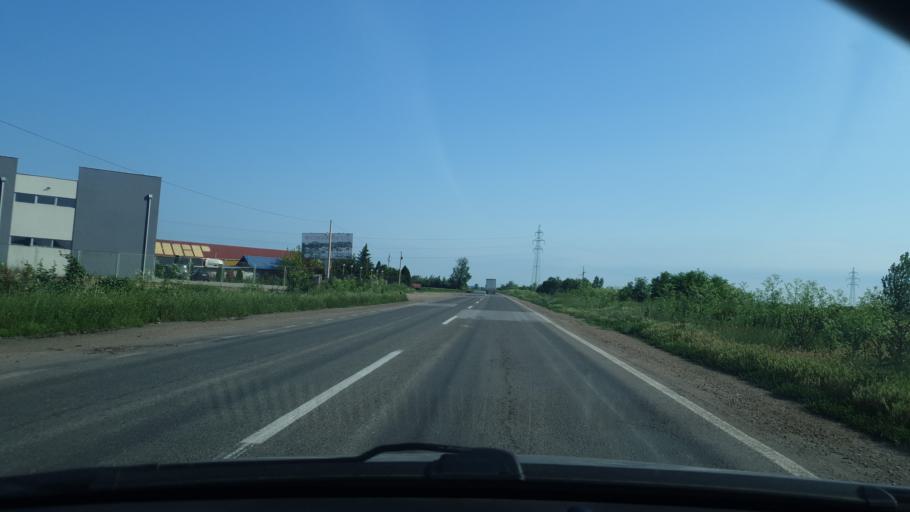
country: RS
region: Central Serbia
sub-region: Podunavski Okrug
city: Smederevo
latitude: 44.6582
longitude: 20.9688
